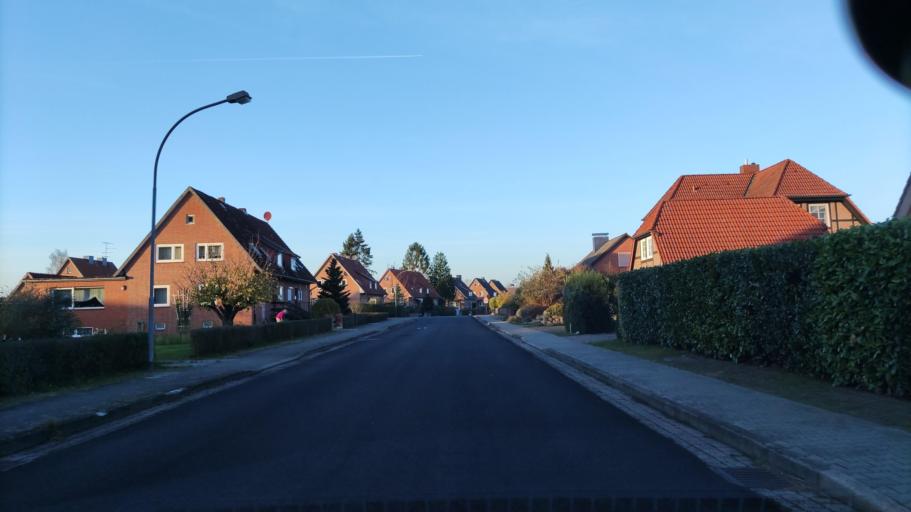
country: DE
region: Lower Saxony
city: Bleckede
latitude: 53.2820
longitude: 10.7316
